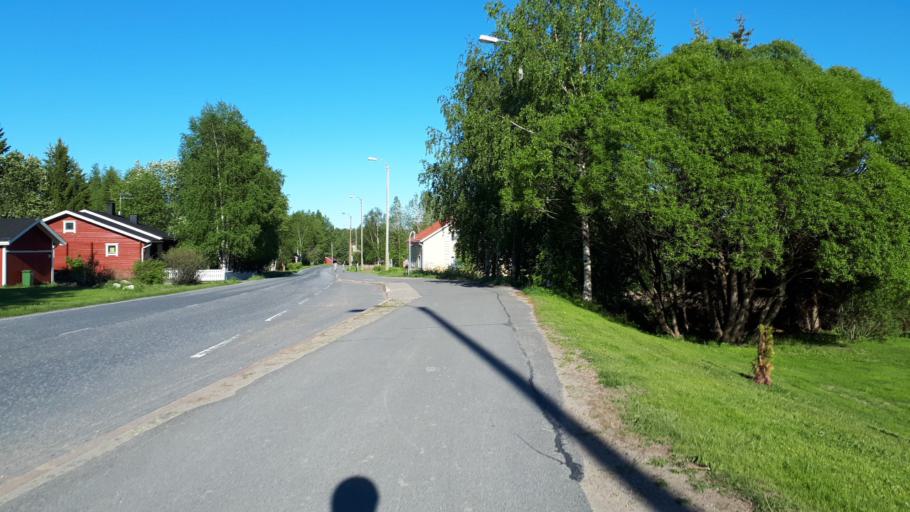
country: FI
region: Northern Ostrobothnia
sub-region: Oulunkaari
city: Ii
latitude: 65.3232
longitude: 25.4472
